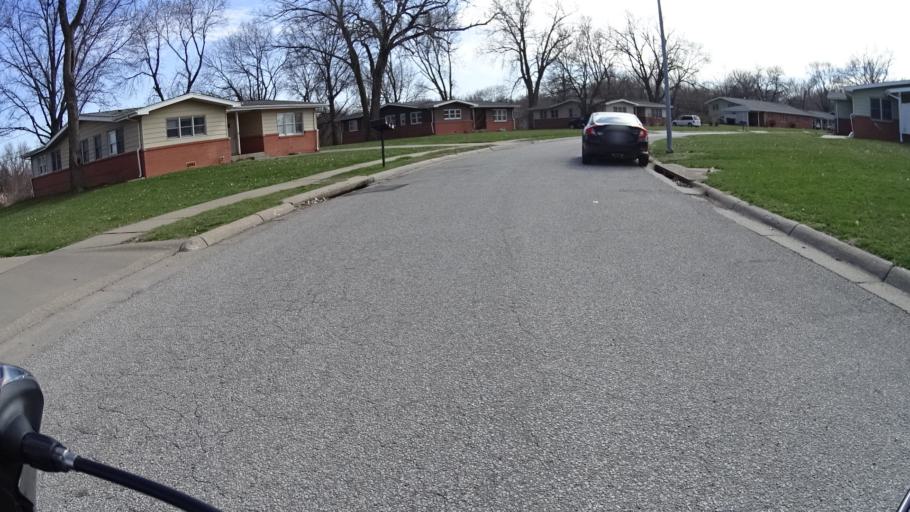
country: US
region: Nebraska
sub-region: Sarpy County
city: Offutt Air Force Base
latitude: 41.1190
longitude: -95.9585
